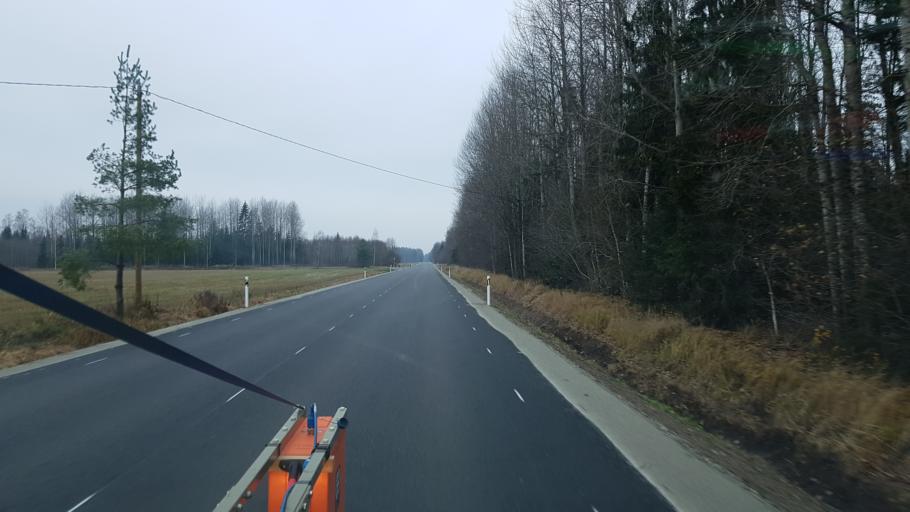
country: EE
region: Paernumaa
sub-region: Vaendra vald (alev)
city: Vandra
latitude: 58.8375
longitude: 25.0773
